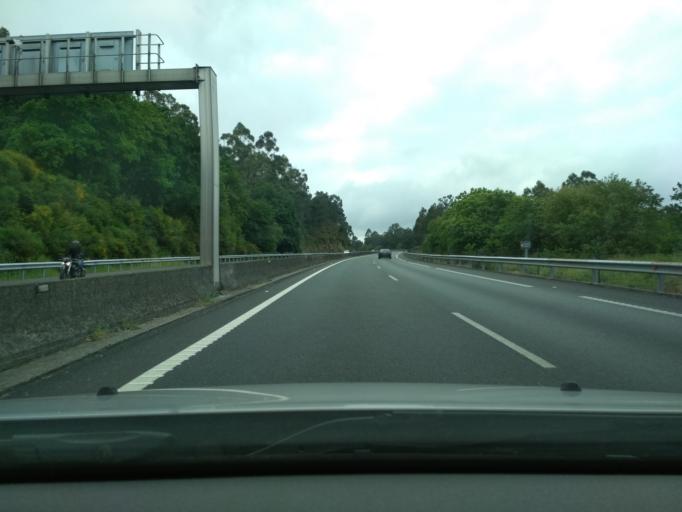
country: ES
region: Galicia
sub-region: Provincia da Coruna
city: Santiago de Compostela
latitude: 42.8488
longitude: -8.5714
